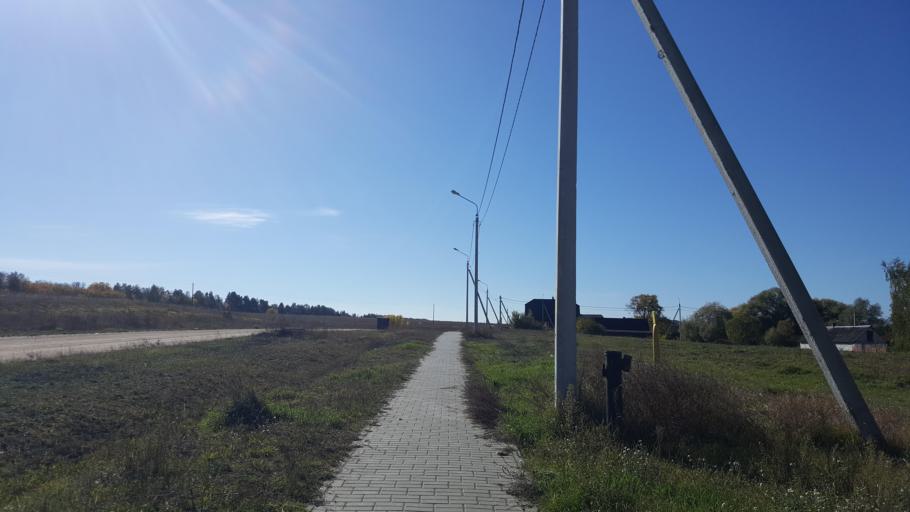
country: BY
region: Brest
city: Kamyanyets
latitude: 52.3882
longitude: 23.8130
